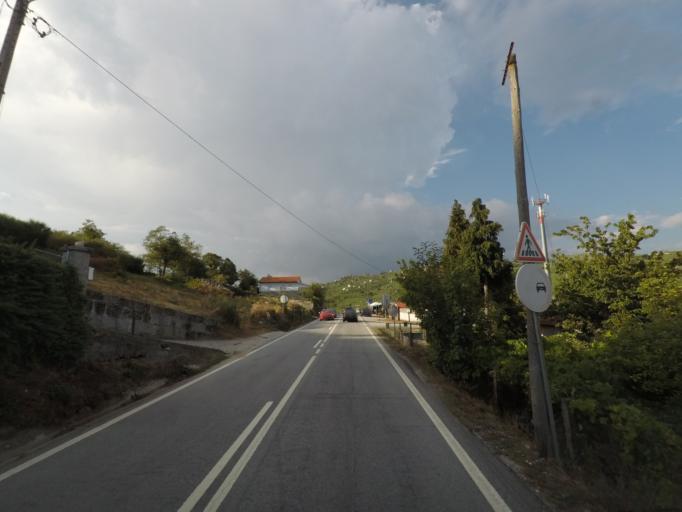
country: PT
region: Porto
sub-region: Baiao
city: Valadares
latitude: 41.1958
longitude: -7.9475
